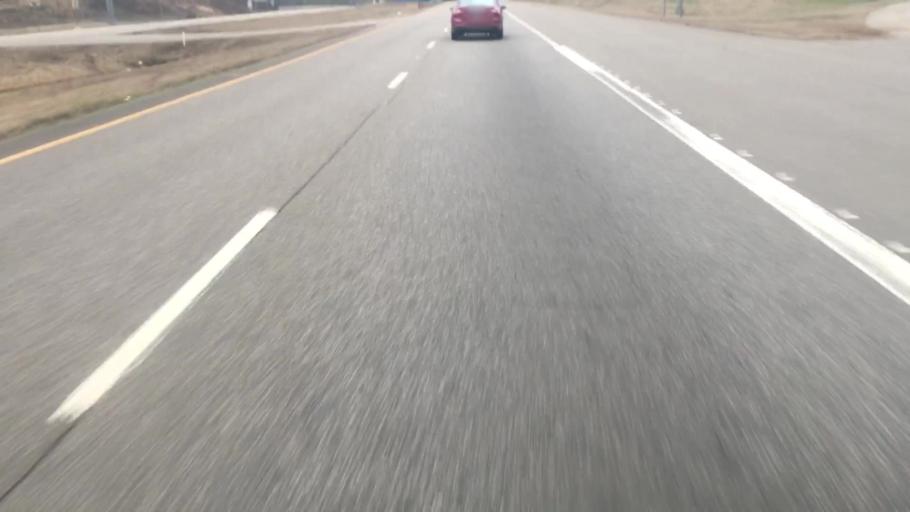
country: US
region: Alabama
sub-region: Jefferson County
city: Graysville
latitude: 33.6478
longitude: -86.9760
